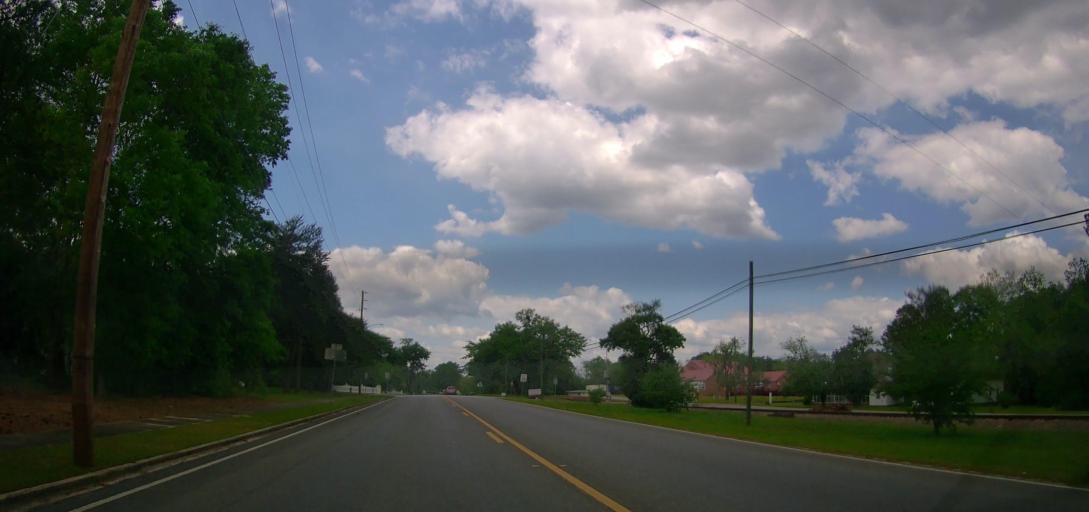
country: US
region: Georgia
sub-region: Treutlen County
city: Soperton
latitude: 32.3723
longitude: -82.5868
